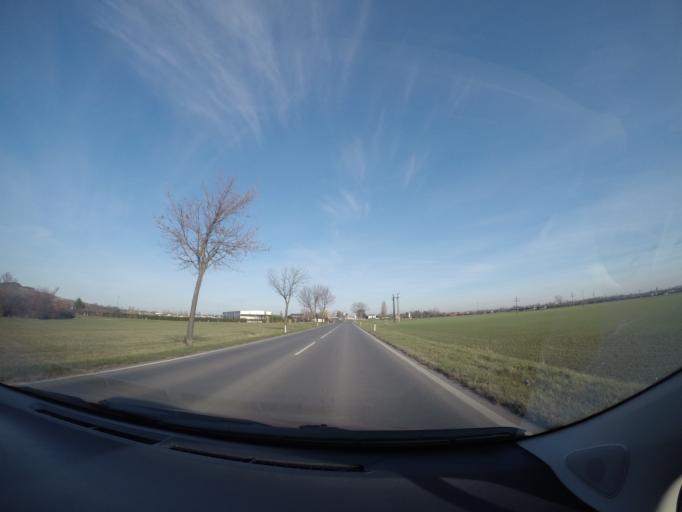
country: AT
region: Lower Austria
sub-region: Politischer Bezirk Baden
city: Traiskirchen
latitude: 48.0338
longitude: 16.2977
